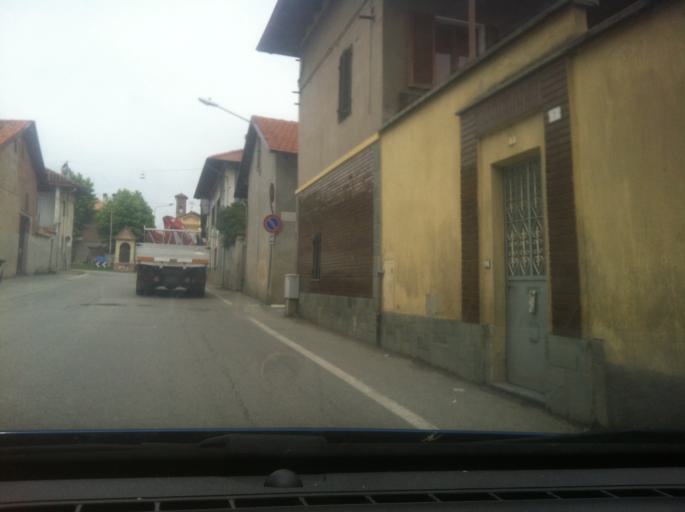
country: IT
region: Piedmont
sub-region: Provincia di Torino
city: Foglizzo
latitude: 45.2711
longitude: 7.8215
